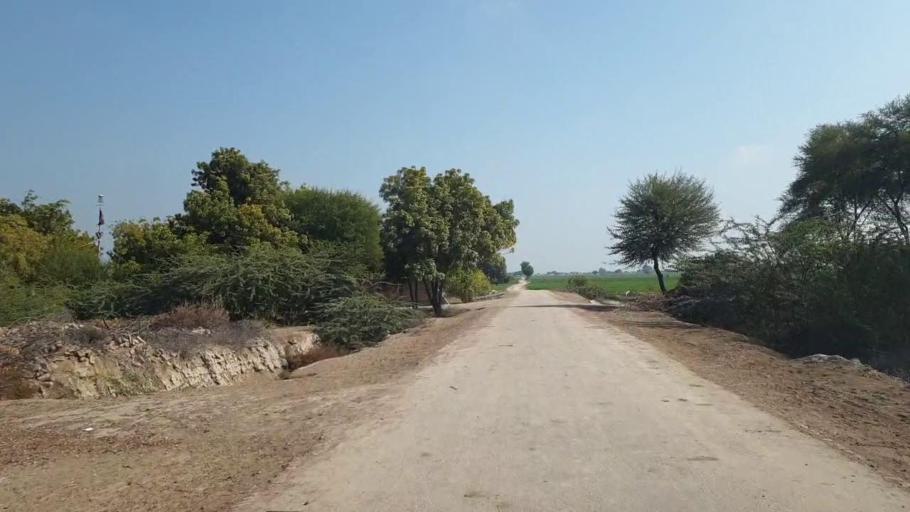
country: PK
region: Sindh
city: Shahdadpur
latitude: 26.0295
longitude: 68.5987
